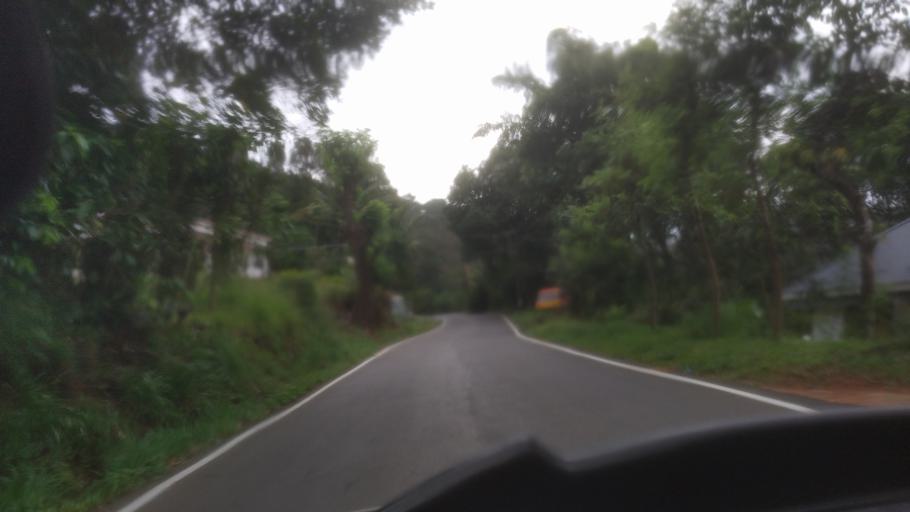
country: IN
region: Kerala
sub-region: Idukki
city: Idukki
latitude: 9.9444
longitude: 77.0195
